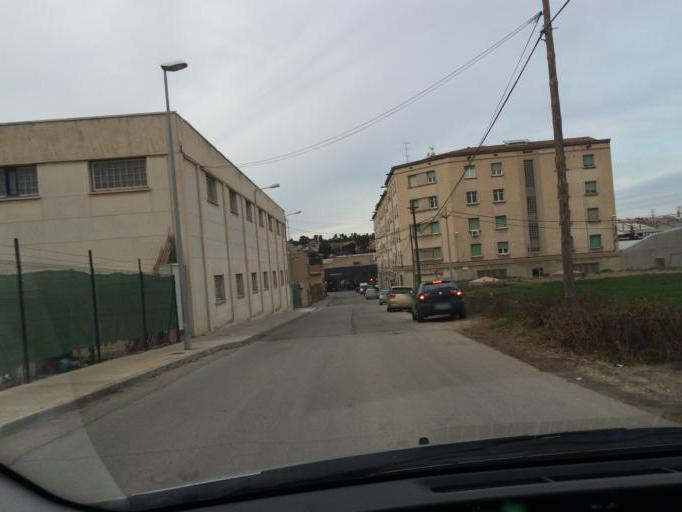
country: ES
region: Catalonia
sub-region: Provincia de Barcelona
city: Manresa
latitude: 41.7324
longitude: 1.8402
